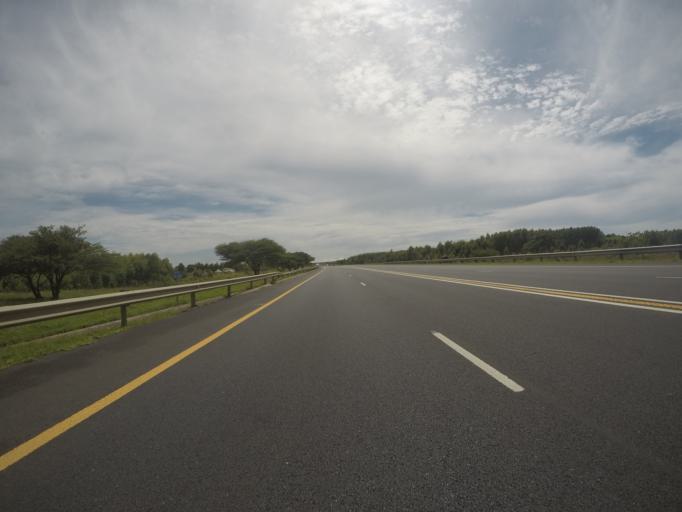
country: ZA
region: KwaZulu-Natal
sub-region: iLembe District Municipality
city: Mandeni
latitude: -29.1595
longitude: 31.5359
